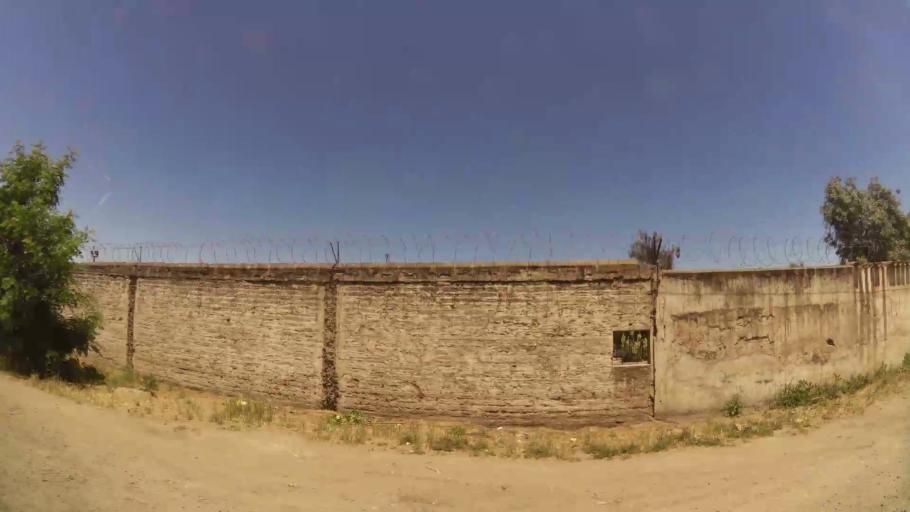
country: CL
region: Santiago Metropolitan
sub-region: Provincia de Maipo
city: San Bernardo
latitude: -33.6040
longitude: -70.6911
